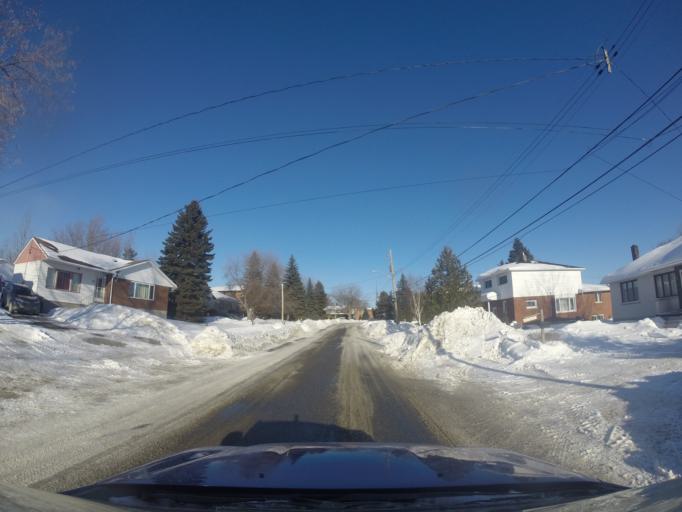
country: CA
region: Ontario
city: Greater Sudbury
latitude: 46.4622
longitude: -80.9949
